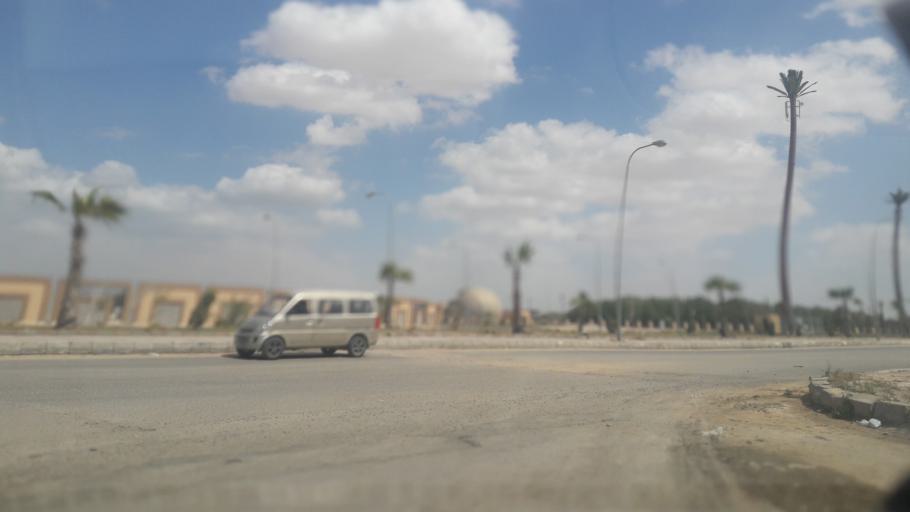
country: EG
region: Al Jizah
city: Madinat Sittah Uktubar
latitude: 29.9363
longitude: 31.0648
